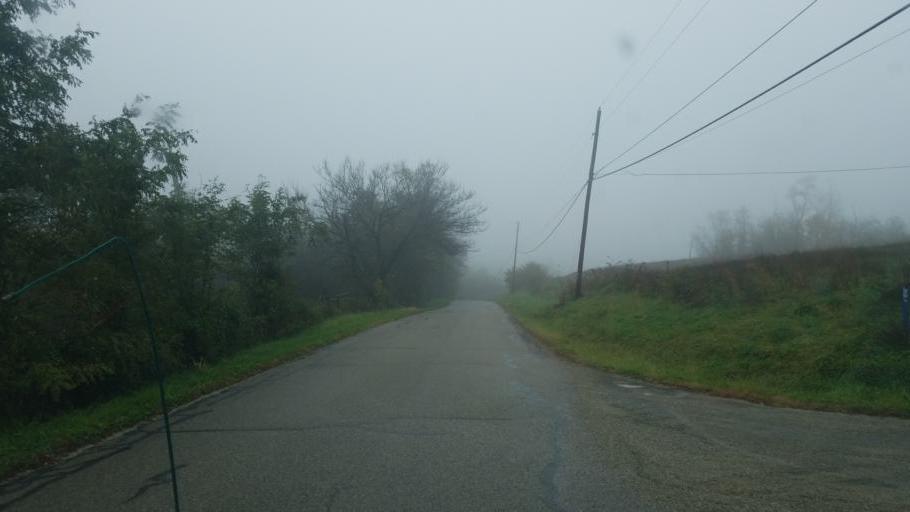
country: US
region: Ohio
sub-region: Morgan County
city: McConnelsville
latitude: 39.6329
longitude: -81.8764
